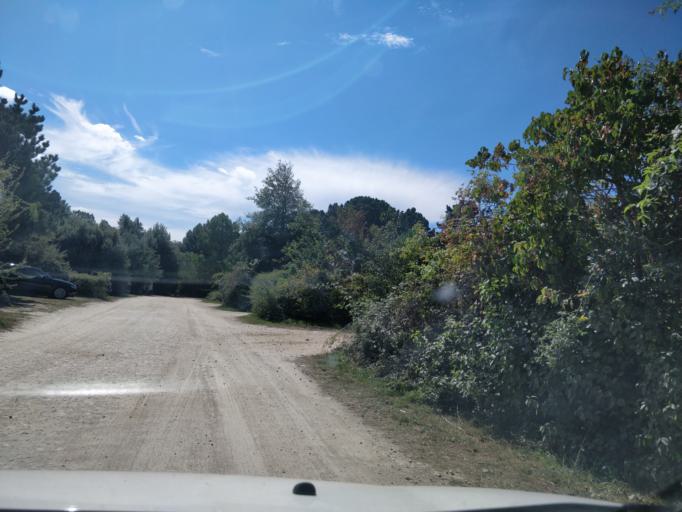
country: FR
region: Brittany
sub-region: Departement du Morbihan
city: Saint-Philibert
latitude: 47.5695
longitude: -3.0005
